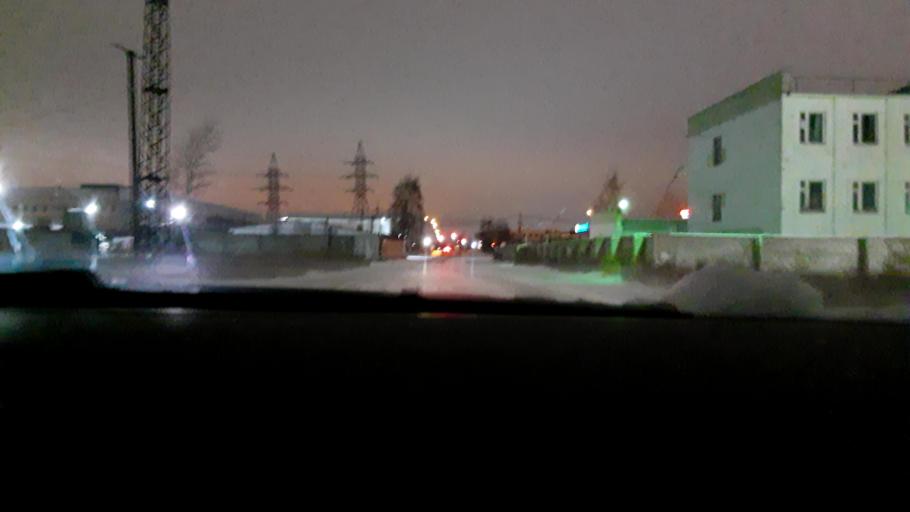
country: RU
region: Nizjnij Novgorod
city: Nizhniy Novgorod
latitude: 56.2482
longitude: 43.9201
